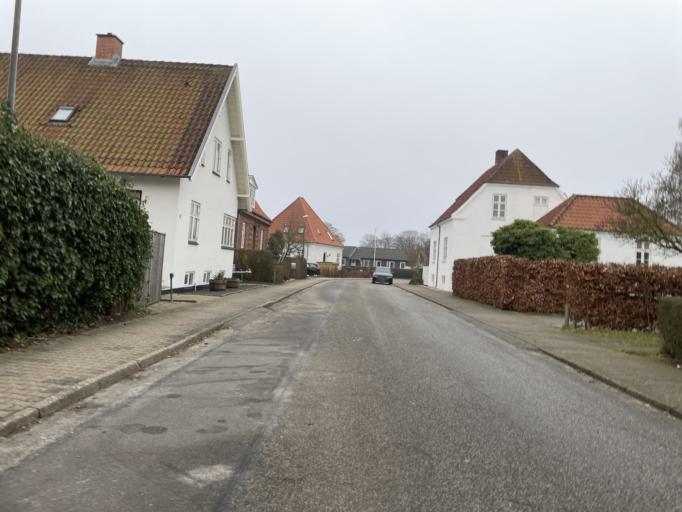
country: DK
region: South Denmark
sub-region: Fredericia Kommune
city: Fredericia
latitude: 55.5721
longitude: 9.7575
